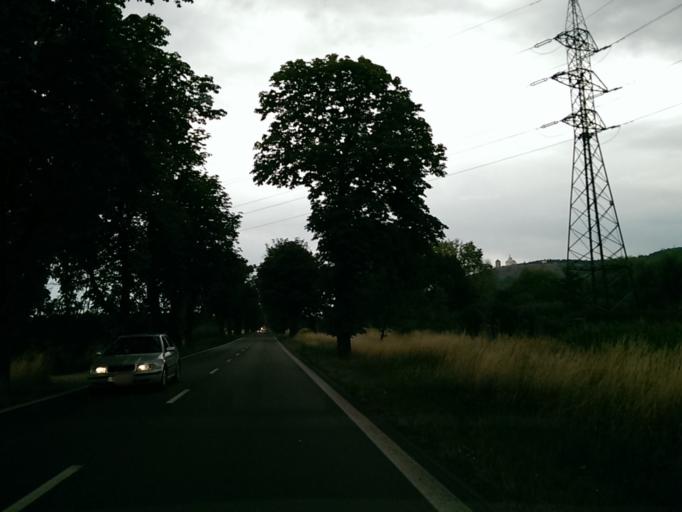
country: CZ
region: South Moravian
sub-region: Okres Breclav
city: Mikulov
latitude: 48.7957
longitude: 16.6603
